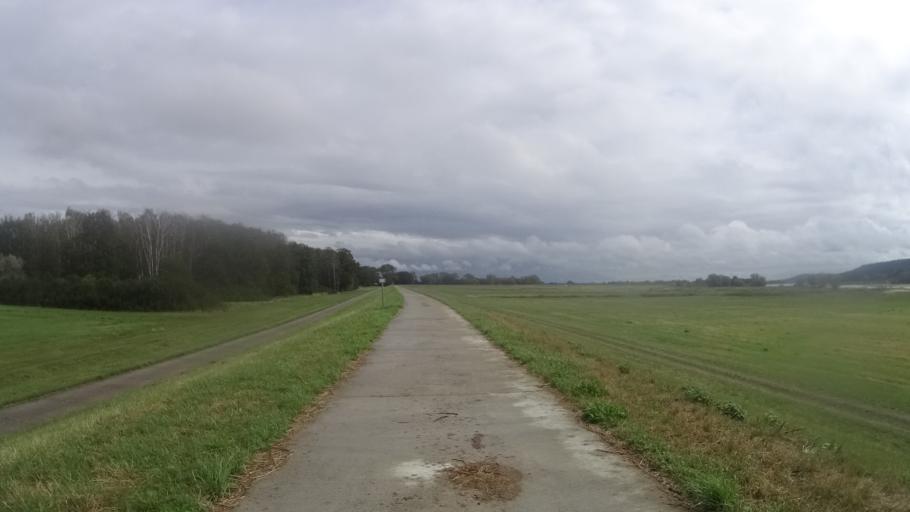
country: DE
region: Lower Saxony
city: Neu Darchau
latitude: 53.2358
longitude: 10.9022
